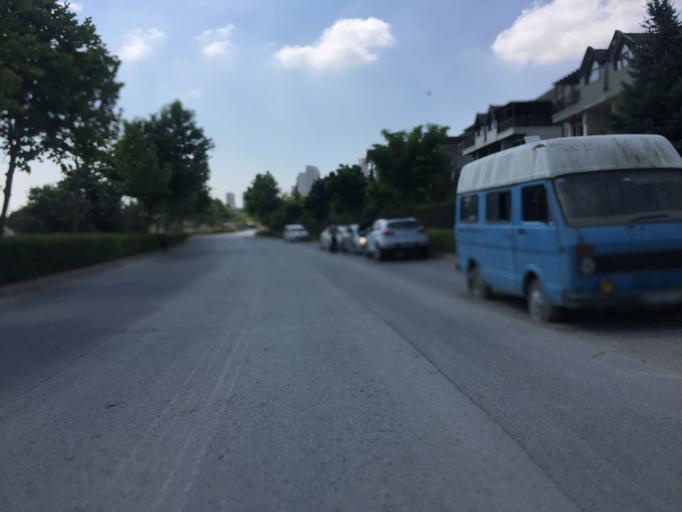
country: TR
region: Istanbul
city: Esenyurt
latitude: 41.0879
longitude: 28.6704
